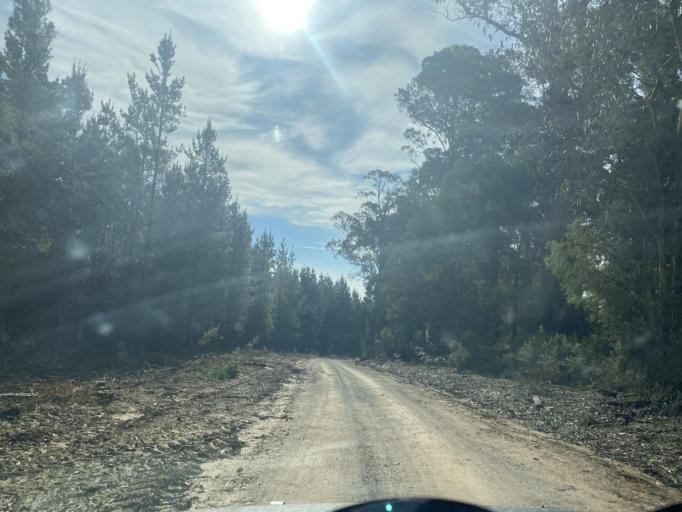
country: AU
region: Victoria
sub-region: Mansfield
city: Mansfield
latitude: -36.8825
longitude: 146.1942
